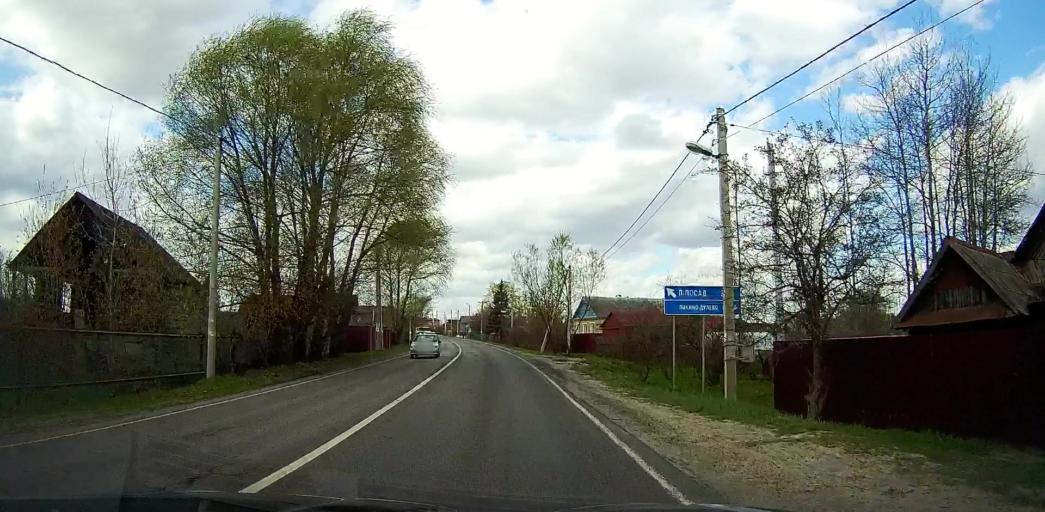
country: RU
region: Moskovskaya
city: Davydovo
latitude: 55.6345
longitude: 38.8692
